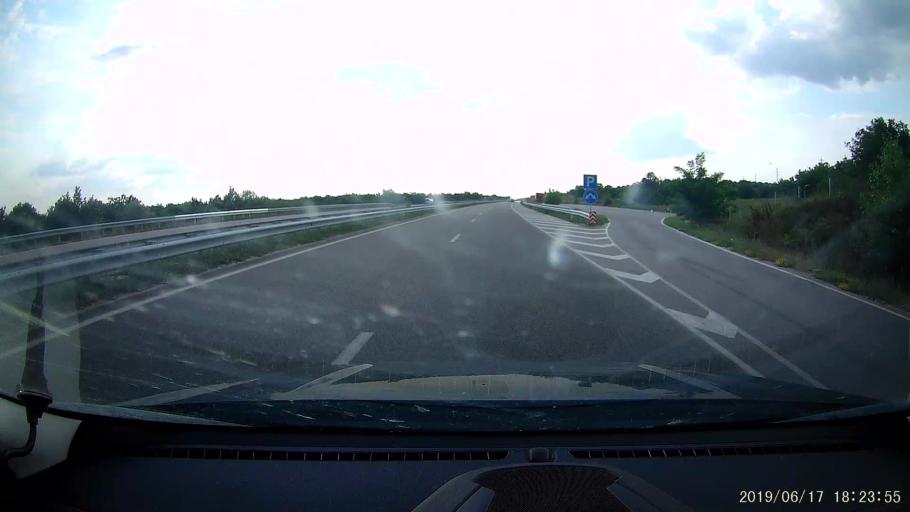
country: BG
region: Khaskovo
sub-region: Obshtina Dimitrovgrad
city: Dimitrovgrad
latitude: 41.9787
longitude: 25.7064
